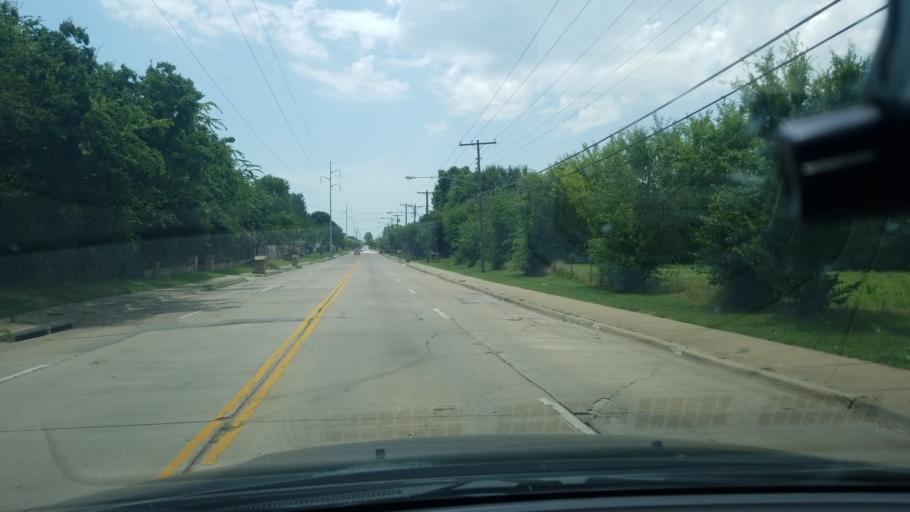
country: US
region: Texas
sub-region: Dallas County
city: Balch Springs
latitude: 32.7467
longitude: -96.6569
